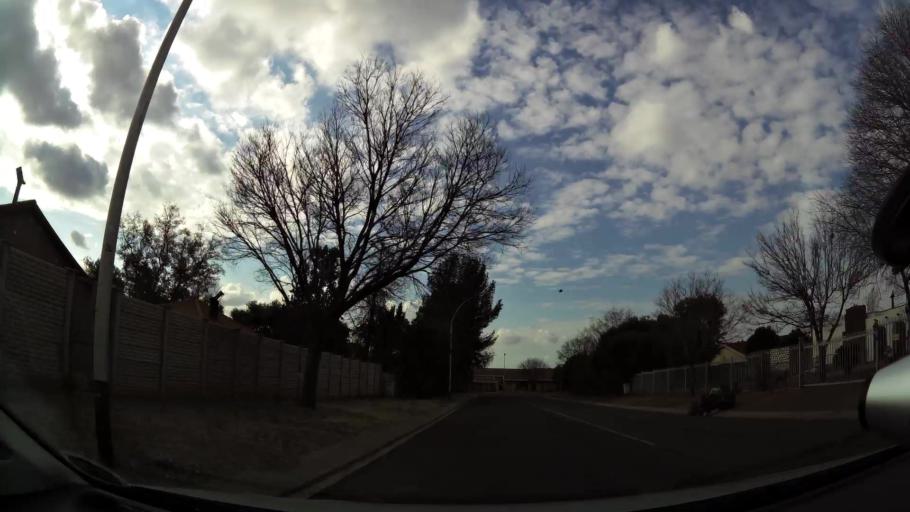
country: ZA
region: Orange Free State
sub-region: Mangaung Metropolitan Municipality
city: Bloemfontein
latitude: -29.0726
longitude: 26.2132
